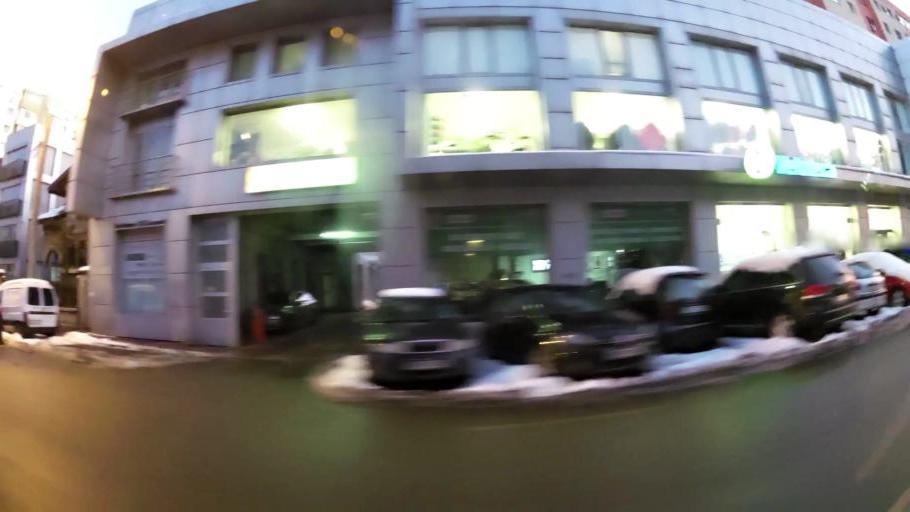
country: RO
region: Bucuresti
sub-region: Municipiul Bucuresti
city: Bucharest
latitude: 44.4447
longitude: 26.1338
